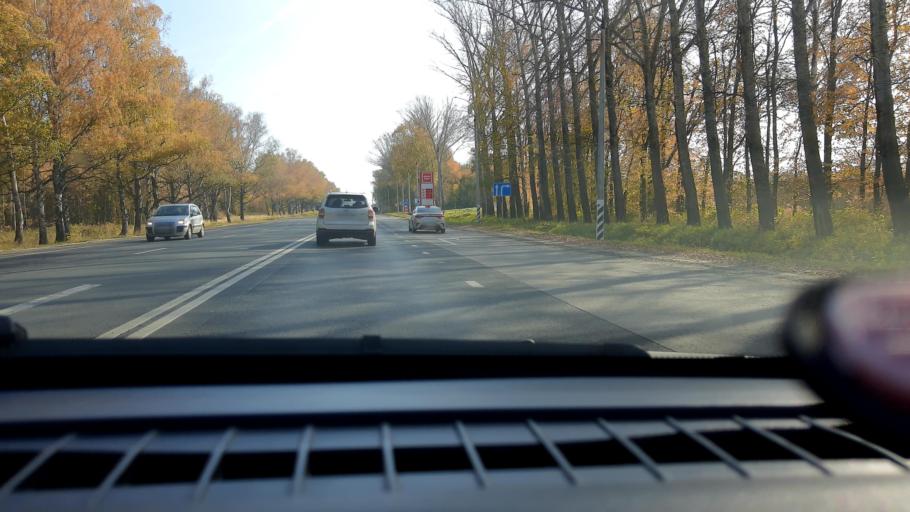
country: RU
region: Nizjnij Novgorod
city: Kstovo
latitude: 56.1376
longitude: 44.2362
